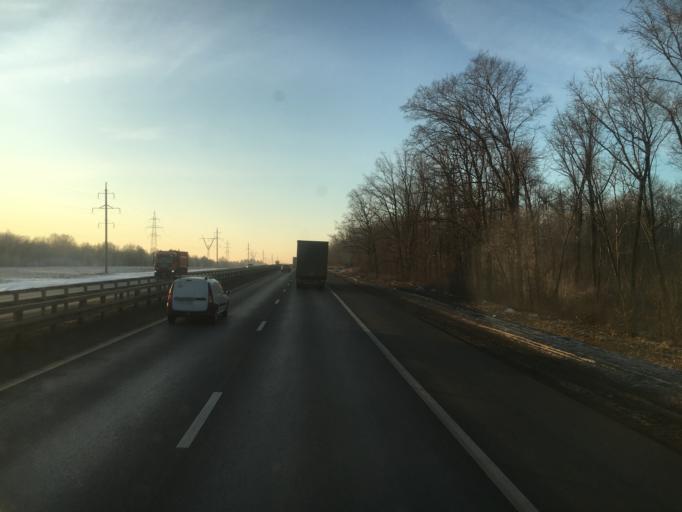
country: RU
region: Samara
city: Pribrezhnyy
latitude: 53.5187
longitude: 49.8126
